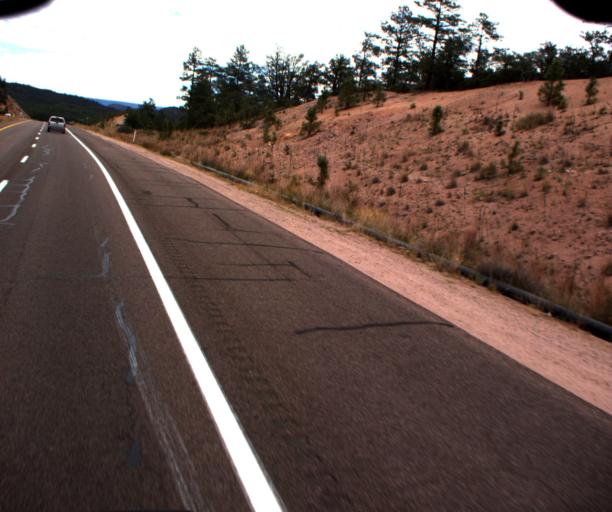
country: US
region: Arizona
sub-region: Gila County
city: Star Valley
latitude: 34.2782
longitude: -111.1573
